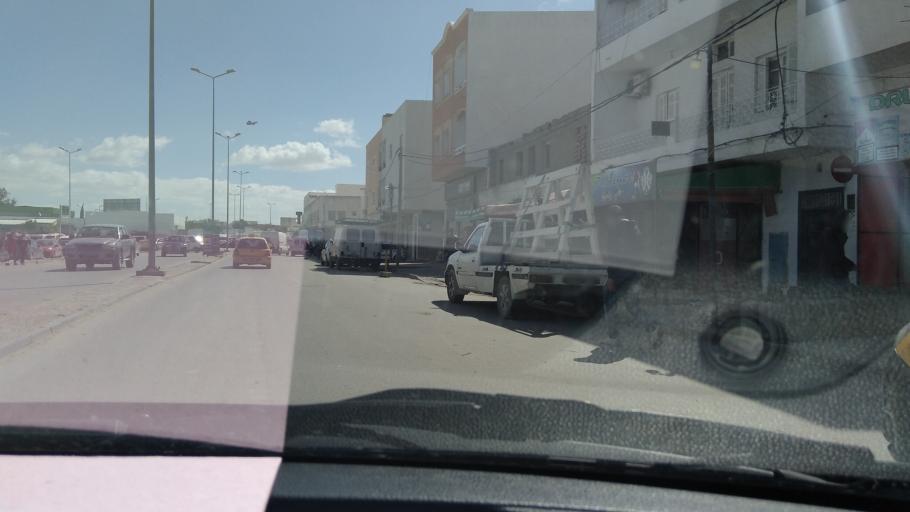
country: TN
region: Al Qayrawan
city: Kairouan
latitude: 35.6805
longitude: 10.0854
